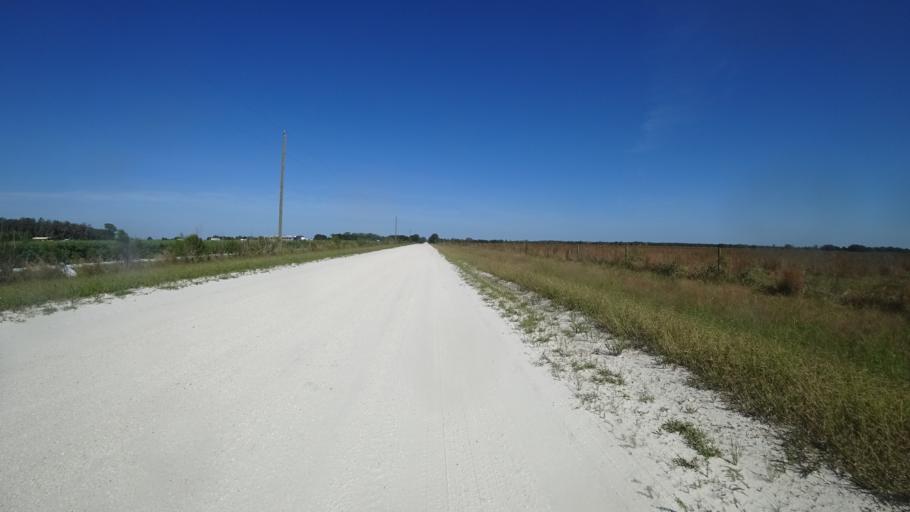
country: US
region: Florida
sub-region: DeSoto County
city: Arcadia
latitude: 27.3077
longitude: -82.0805
